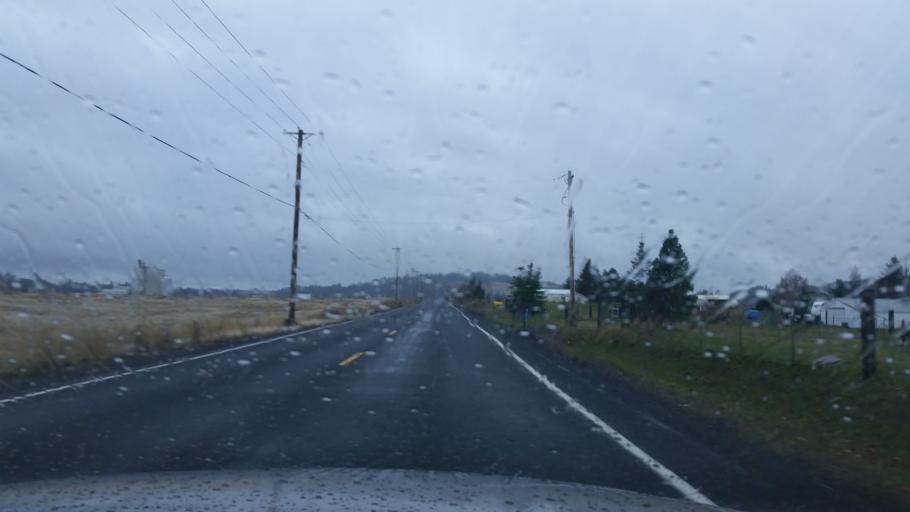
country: US
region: Washington
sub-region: Spokane County
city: Fairchild Air Force Base
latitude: 47.5827
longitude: -117.6076
